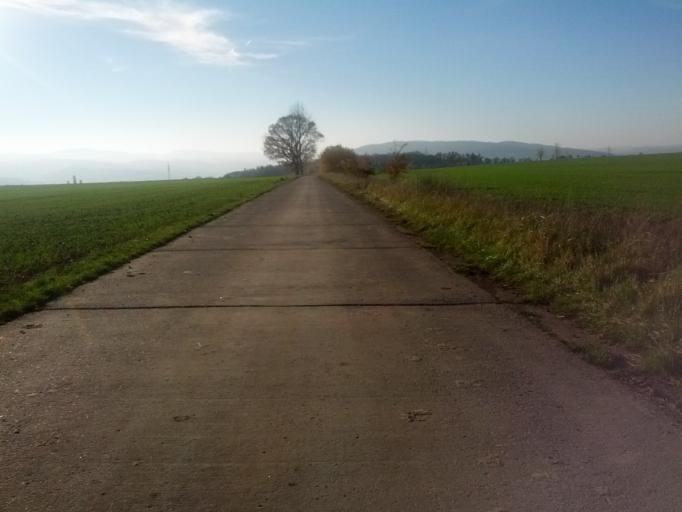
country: DE
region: Thuringia
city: Mechterstadt
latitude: 50.9597
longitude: 10.5362
